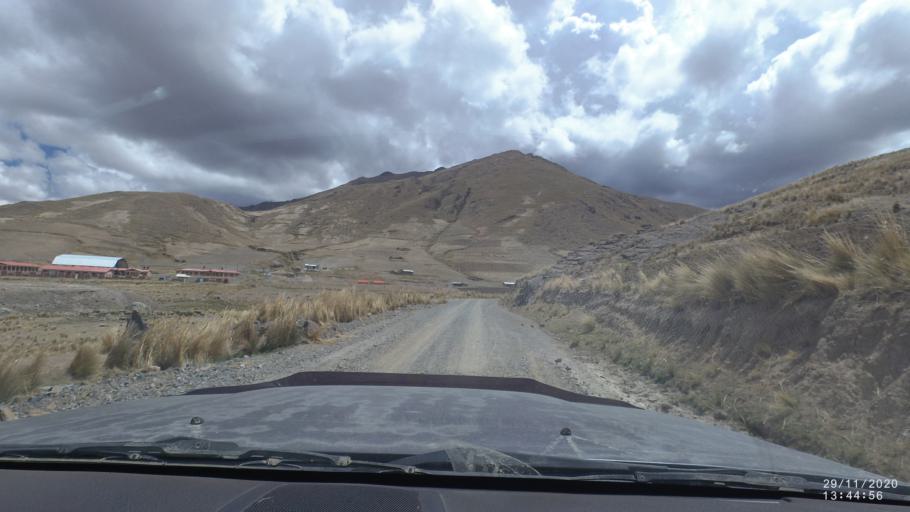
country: BO
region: Cochabamba
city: Cochabamba
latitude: -17.1473
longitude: -66.3185
